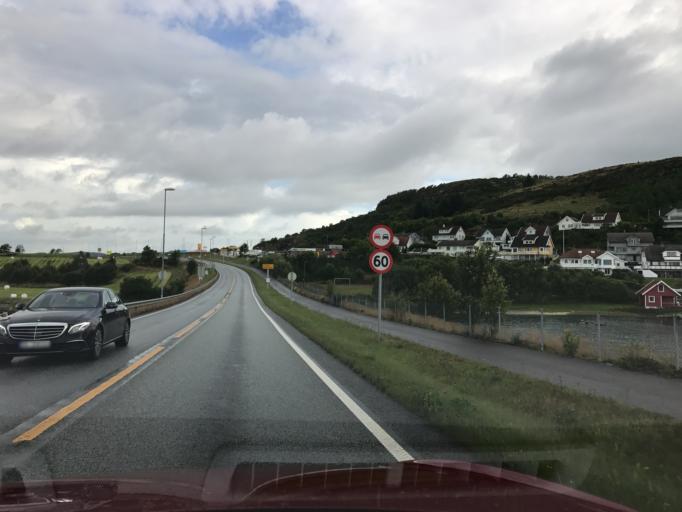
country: NO
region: Rogaland
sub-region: Rennesoy
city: Vikevag
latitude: 59.0613
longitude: 5.6772
